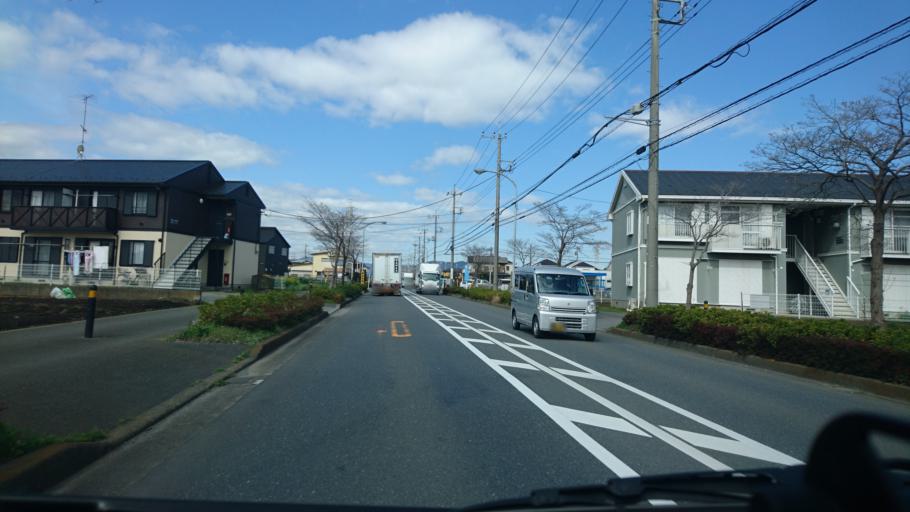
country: JP
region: Kanagawa
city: Zama
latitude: 35.5261
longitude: 139.3431
